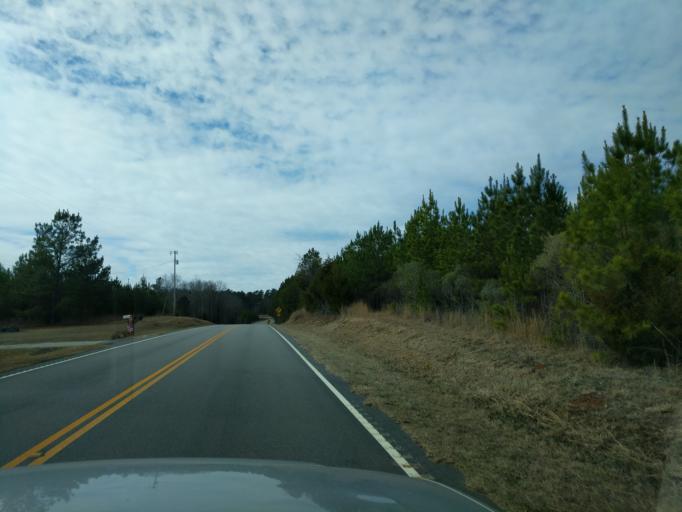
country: US
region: South Carolina
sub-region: Edgefield County
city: Edgefield
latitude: 33.9283
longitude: -82.0038
